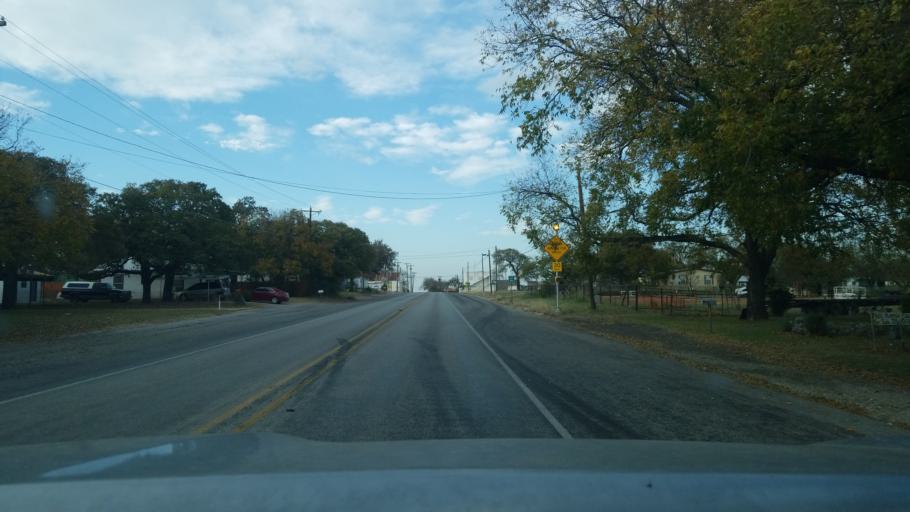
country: US
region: Texas
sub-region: Brown County
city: Lake Brownwood
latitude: 31.9770
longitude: -98.9204
